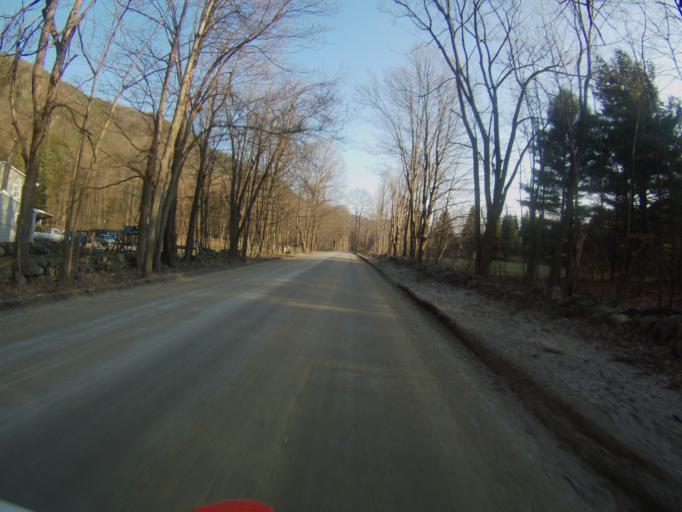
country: US
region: Vermont
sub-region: Addison County
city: Bristol
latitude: 44.1065
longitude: -73.0757
